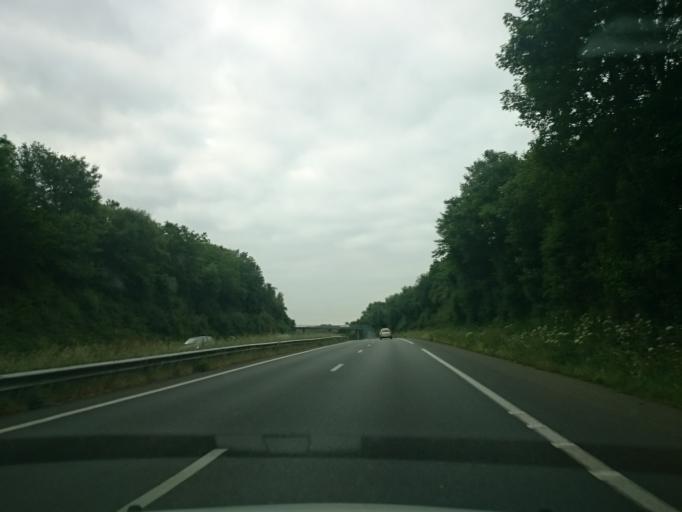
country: FR
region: Brittany
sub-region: Departement du Finistere
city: Daoulas
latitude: 48.3624
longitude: -4.2536
